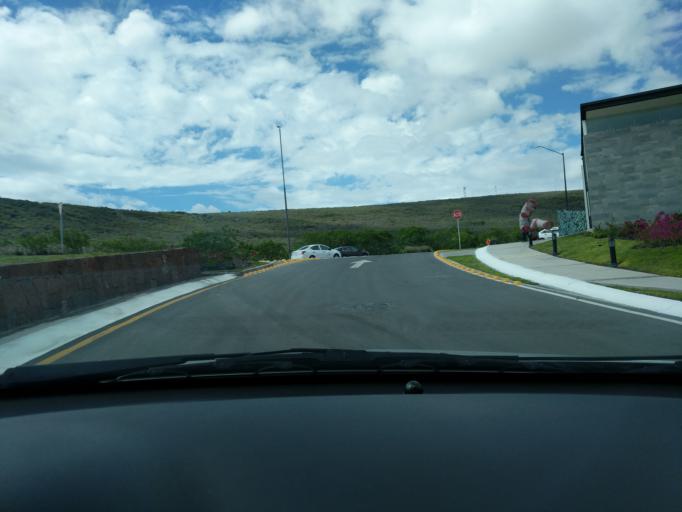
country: MX
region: Queretaro
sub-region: El Marques
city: La Pradera
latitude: 20.6587
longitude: -100.3543
